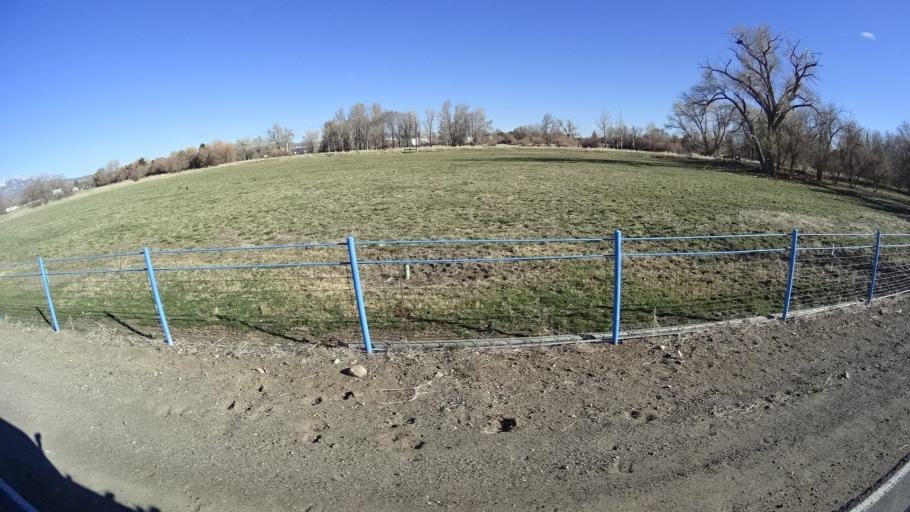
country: US
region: Nevada
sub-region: Washoe County
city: Sparks
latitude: 39.5113
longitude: -119.7349
